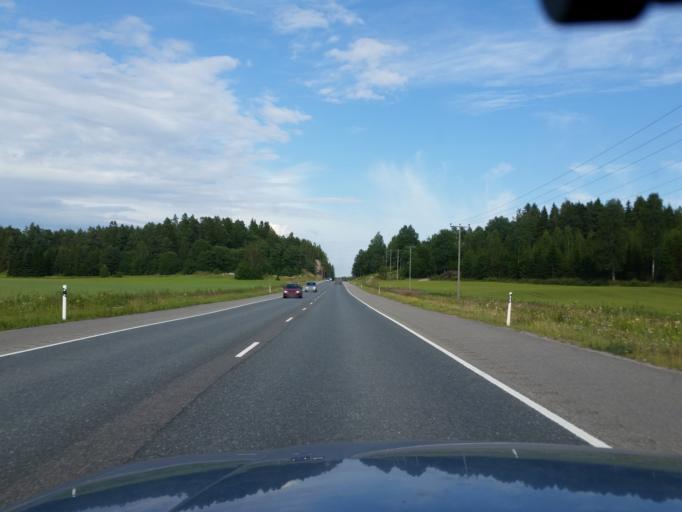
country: FI
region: Uusimaa
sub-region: Helsinki
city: Siuntio
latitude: 60.0855
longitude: 24.1938
